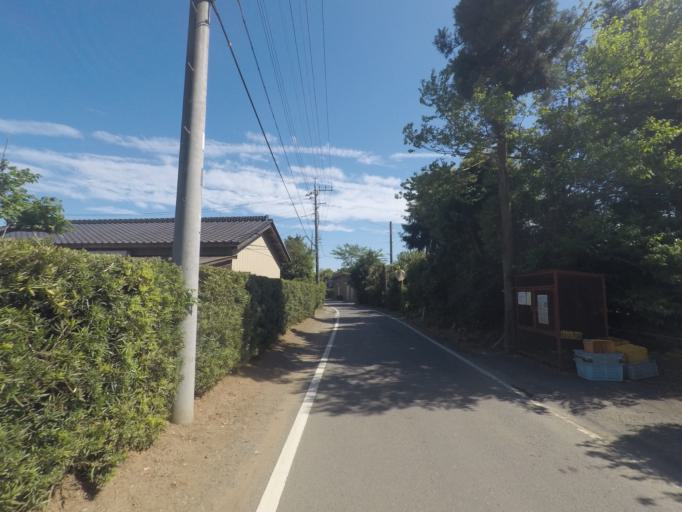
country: JP
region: Ibaraki
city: Itako
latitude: 36.0261
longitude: 140.4710
